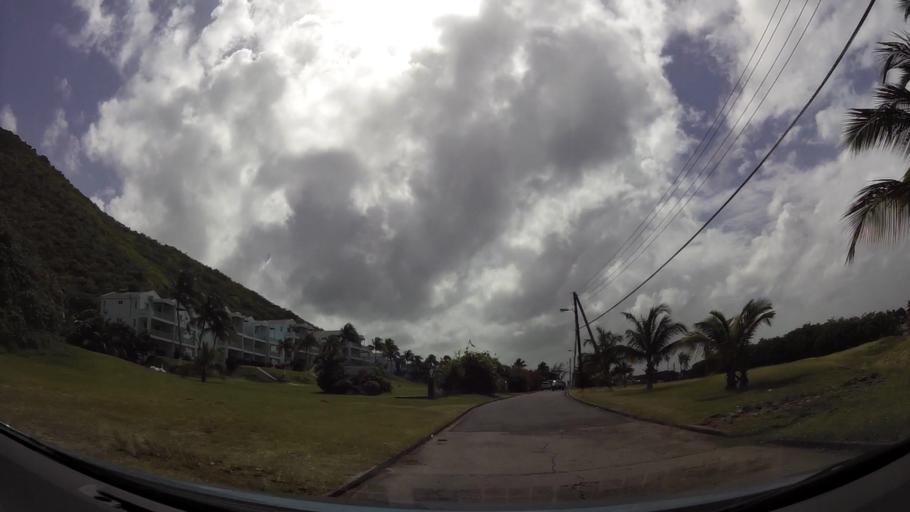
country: KN
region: Saint George Basseterre
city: Basseterre
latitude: 17.2821
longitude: -62.6858
